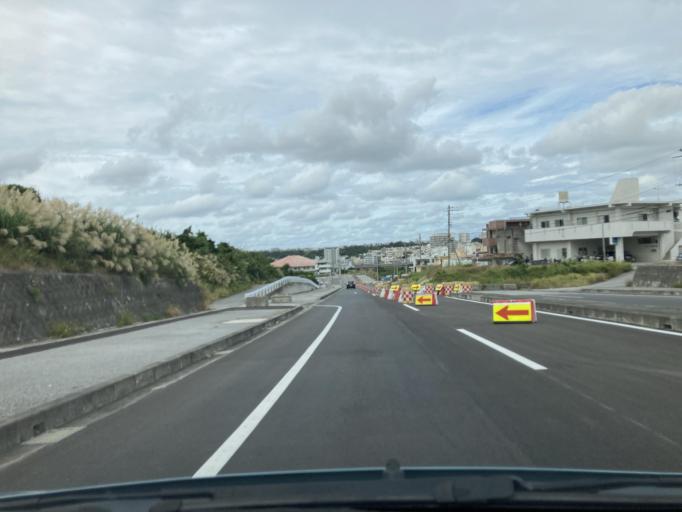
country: JP
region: Okinawa
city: Tomigusuku
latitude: 26.1702
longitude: 127.6769
